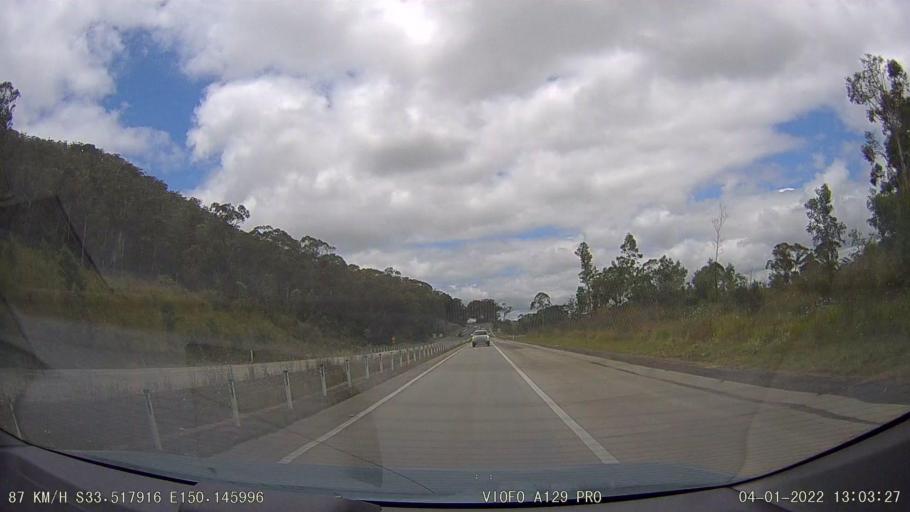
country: AU
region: New South Wales
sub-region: Lithgow
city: Bowenfels
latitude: -33.5176
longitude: 150.1457
